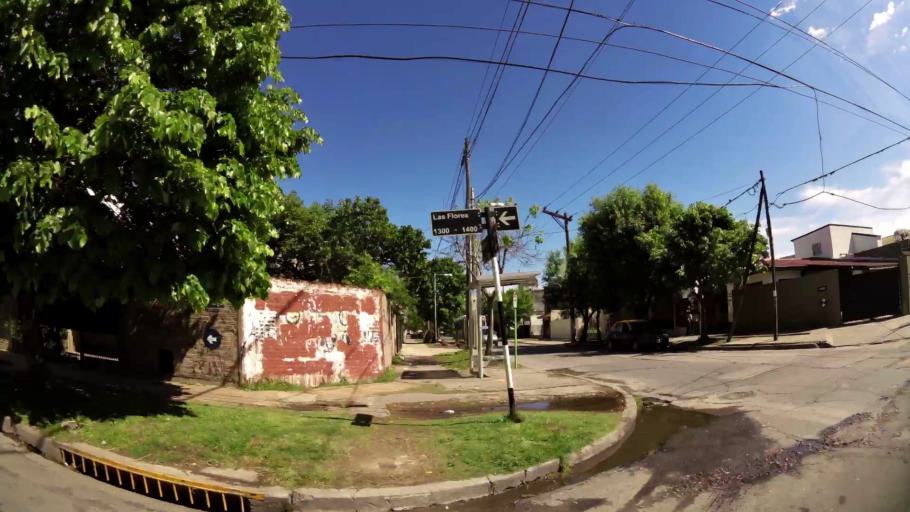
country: AR
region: Buenos Aires
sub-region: Partido de Quilmes
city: Quilmes
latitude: -34.6924
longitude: -58.3044
